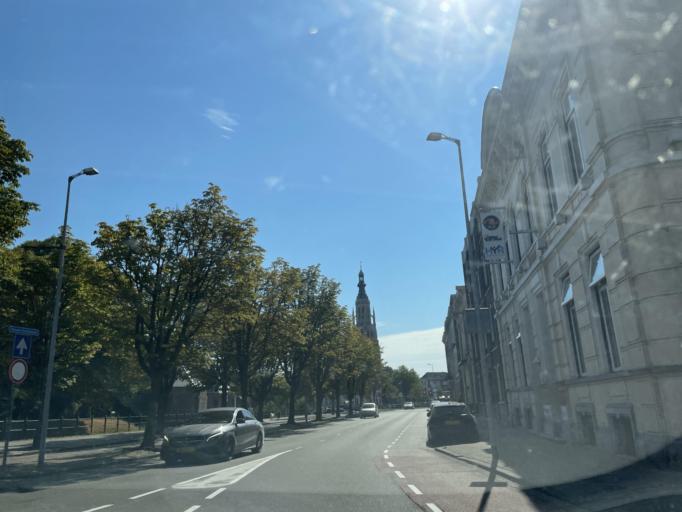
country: NL
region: North Brabant
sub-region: Gemeente Breda
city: Breda
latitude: 51.5914
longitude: 4.7715
